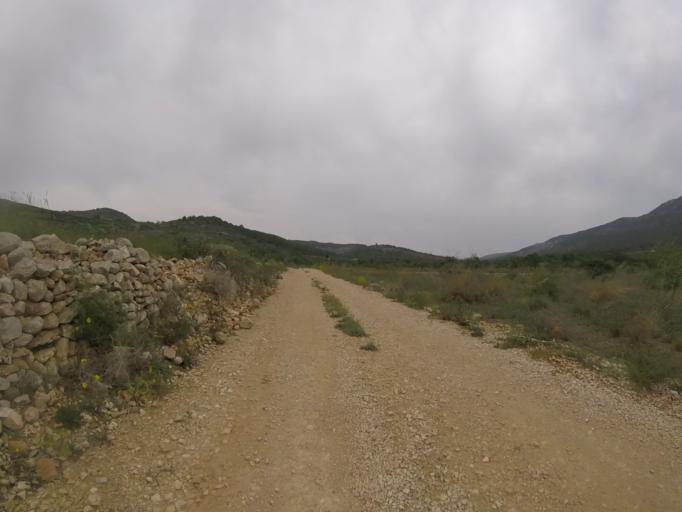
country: ES
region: Valencia
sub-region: Provincia de Castello
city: Alcala de Xivert
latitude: 40.2905
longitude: 0.2602
